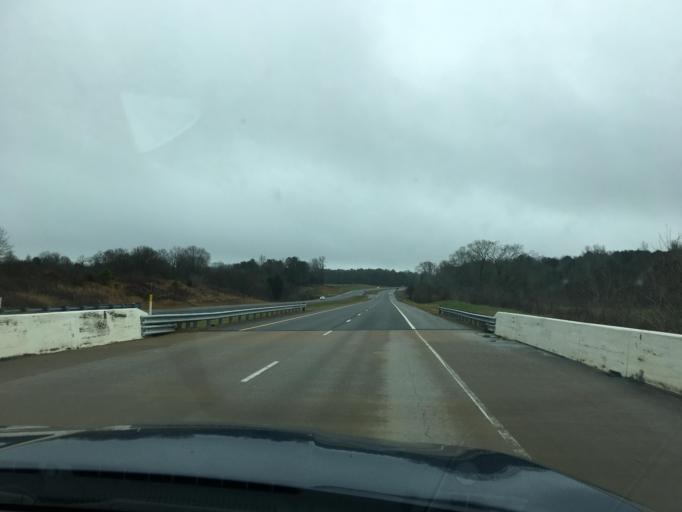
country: US
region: Tennessee
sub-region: McMinn County
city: Athens
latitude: 35.3877
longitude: -84.5643
